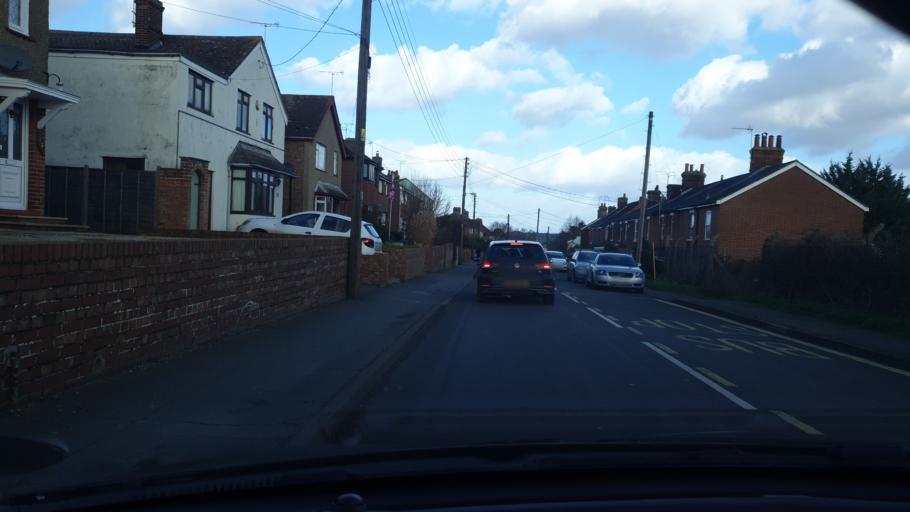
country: GB
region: England
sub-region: Essex
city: Manningtree
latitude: 51.9418
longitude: 1.0579
